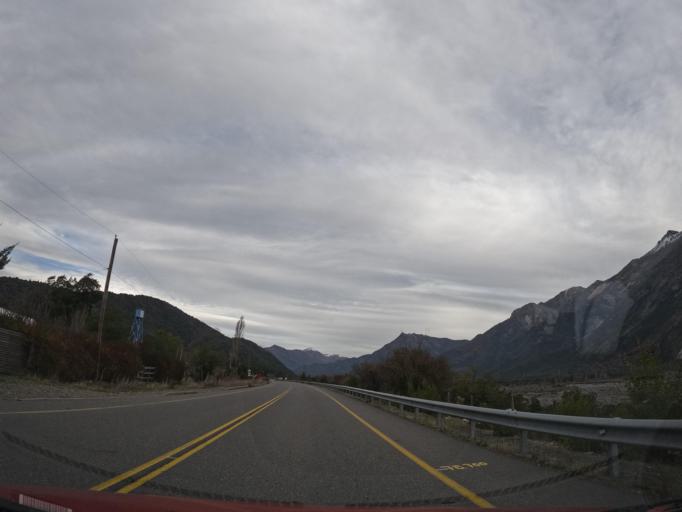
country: CL
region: Maule
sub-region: Provincia de Linares
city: Colbun
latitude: -35.7633
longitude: -71.0020
